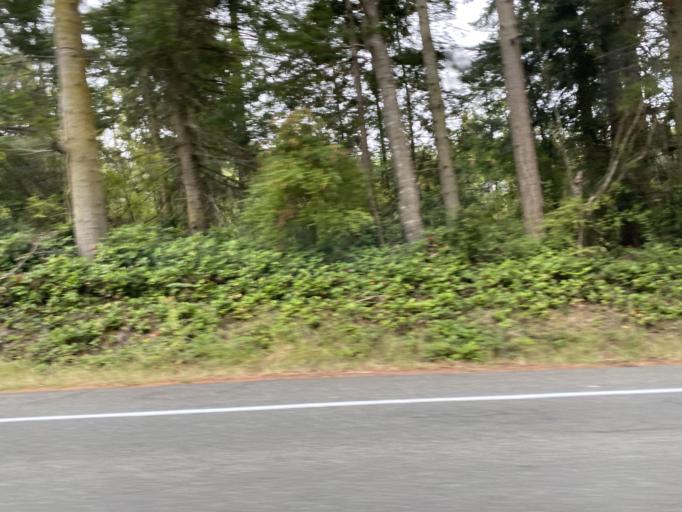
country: US
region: Washington
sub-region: Island County
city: Coupeville
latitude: 48.2196
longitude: -122.6421
